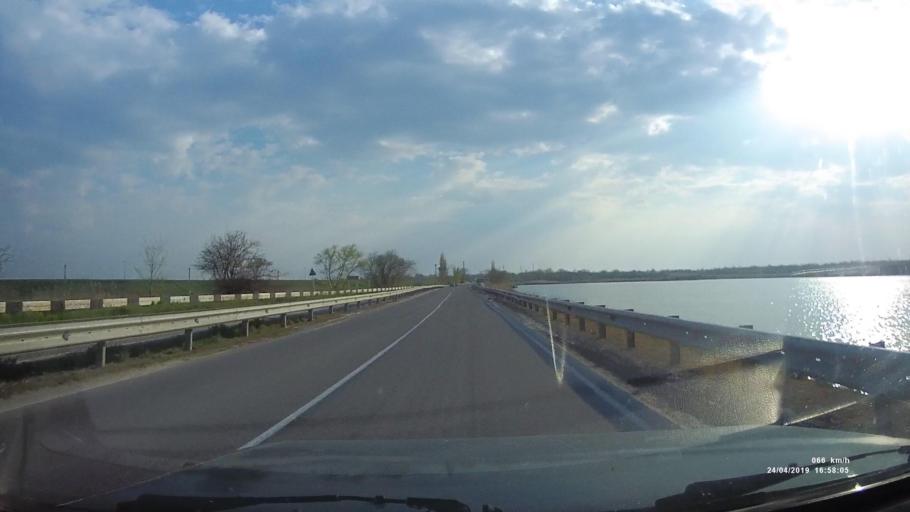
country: RU
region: Rostov
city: Proletarsk
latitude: 46.6309
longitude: 41.6632
